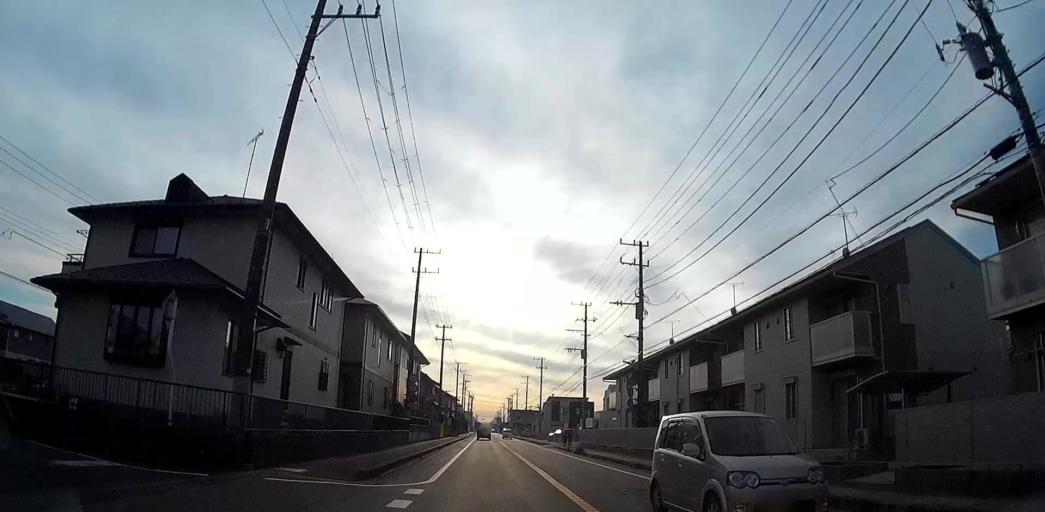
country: JP
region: Chiba
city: Hasaki
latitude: 35.7952
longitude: 140.7748
